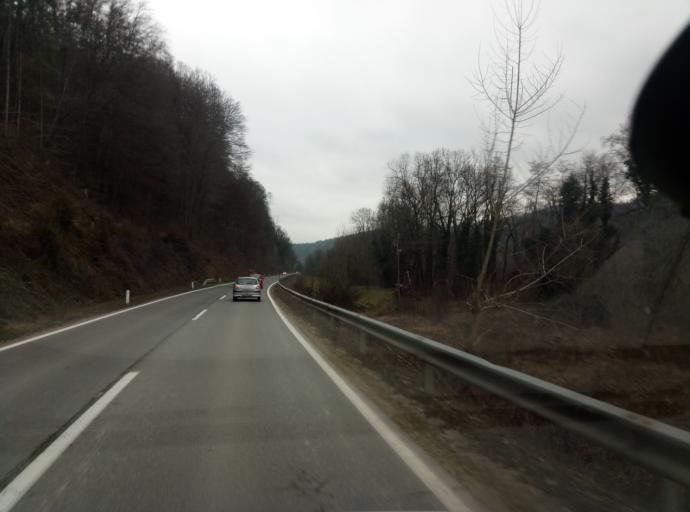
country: SI
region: Litija
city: Litija
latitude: 46.1010
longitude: 14.7993
